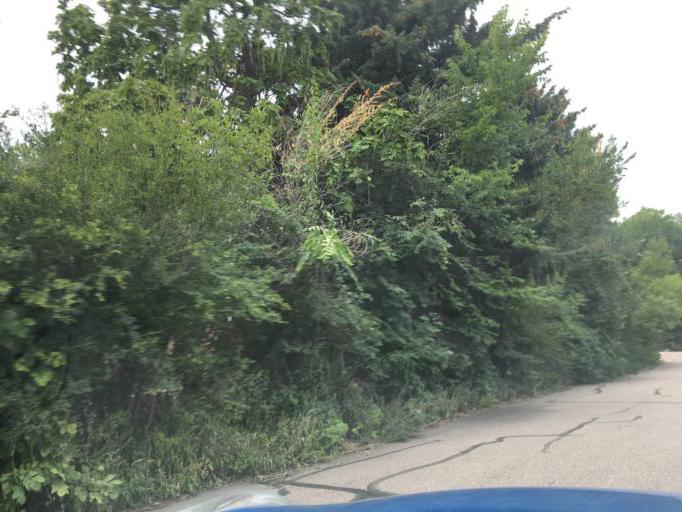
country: US
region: Colorado
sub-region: Jefferson County
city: Wheat Ridge
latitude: 39.7490
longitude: -105.0932
